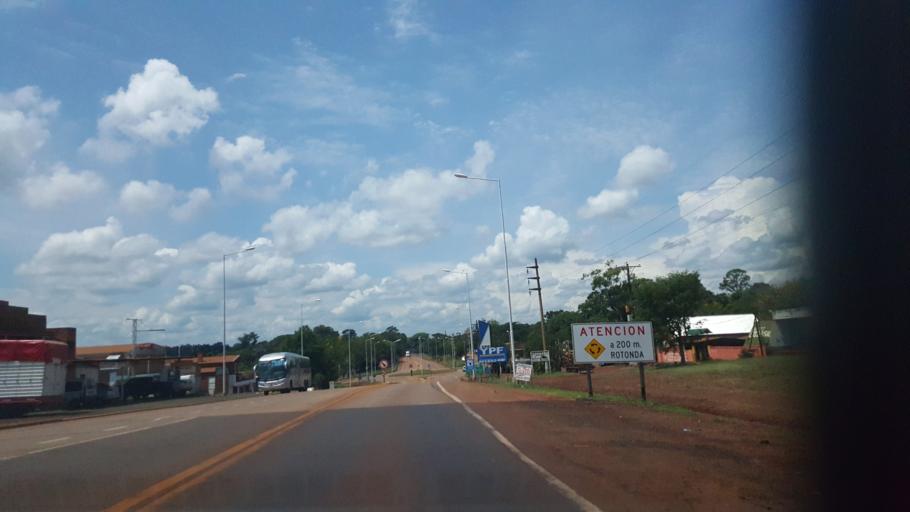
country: AR
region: Misiones
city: Puerto Rico
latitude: -26.8208
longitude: -55.0250
